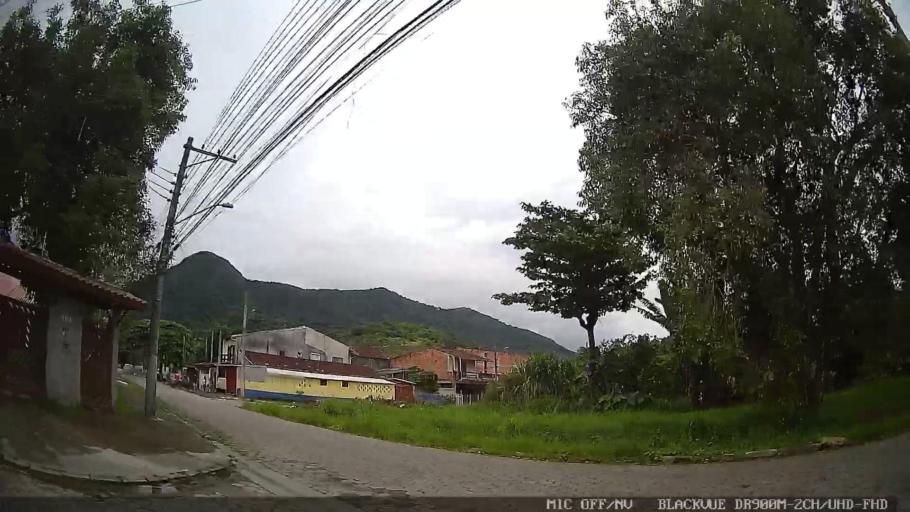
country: BR
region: Sao Paulo
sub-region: Caraguatatuba
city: Caraguatatuba
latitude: -23.6183
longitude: -45.3864
